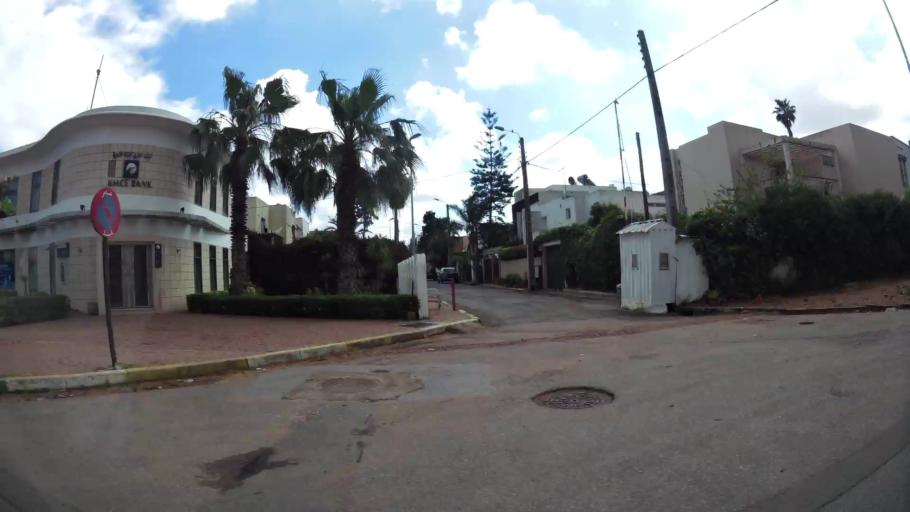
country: MA
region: Grand Casablanca
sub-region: Casablanca
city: Casablanca
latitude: 33.5556
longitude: -7.6109
